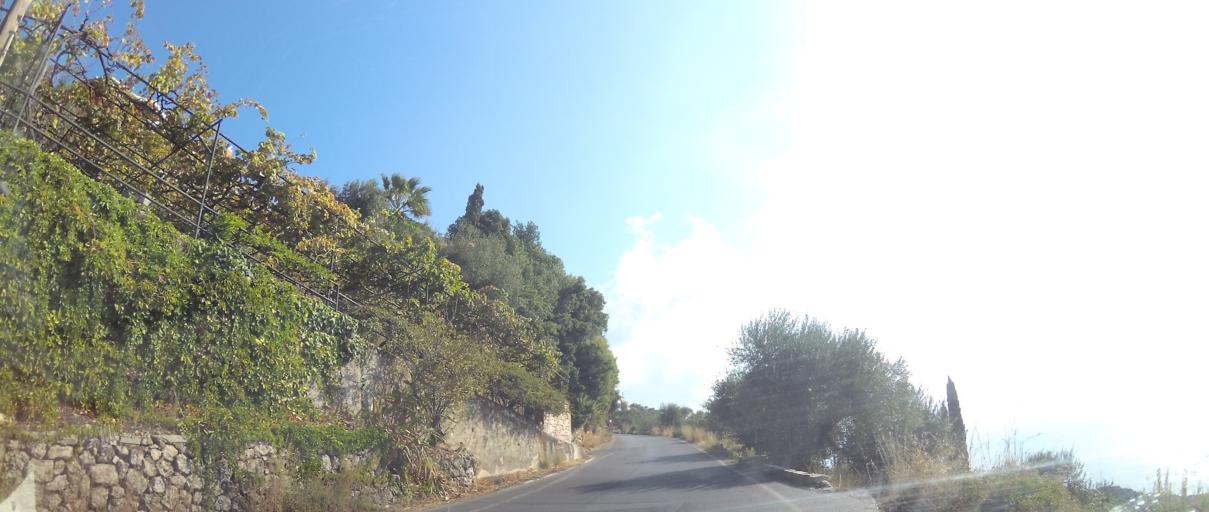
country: GR
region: Ionian Islands
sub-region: Nomos Kerkyras
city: Kontokali
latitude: 39.7176
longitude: 19.8443
